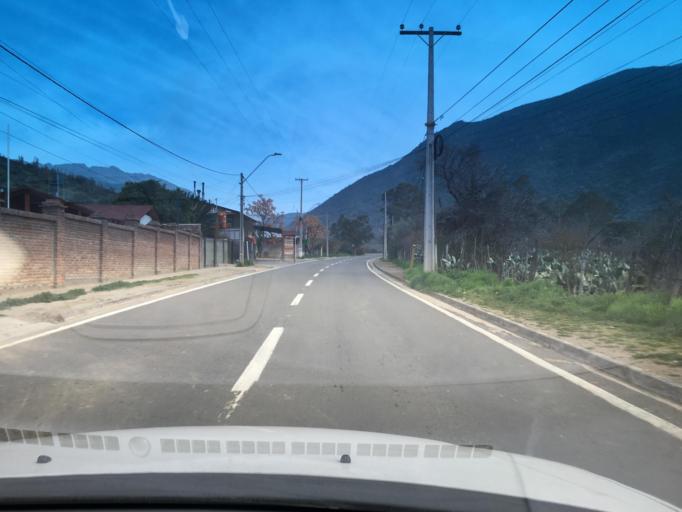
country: CL
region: Santiago Metropolitan
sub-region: Provincia de Chacabuco
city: Lampa
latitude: -33.0753
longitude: -70.9318
